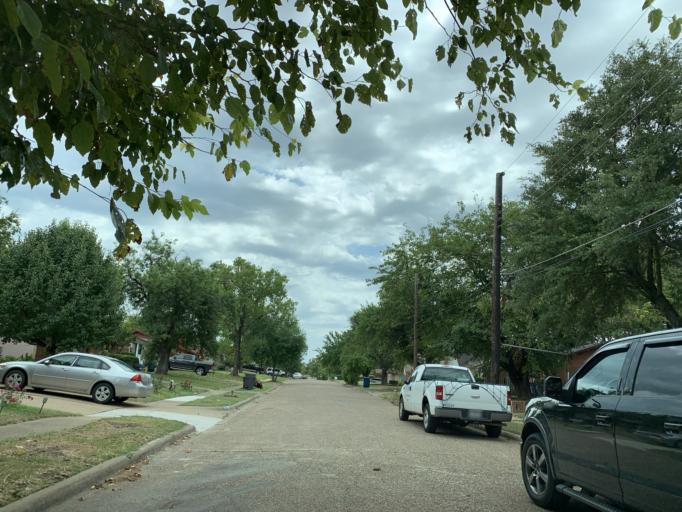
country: US
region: Texas
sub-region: Dallas County
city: DeSoto
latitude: 32.6563
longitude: -96.8253
